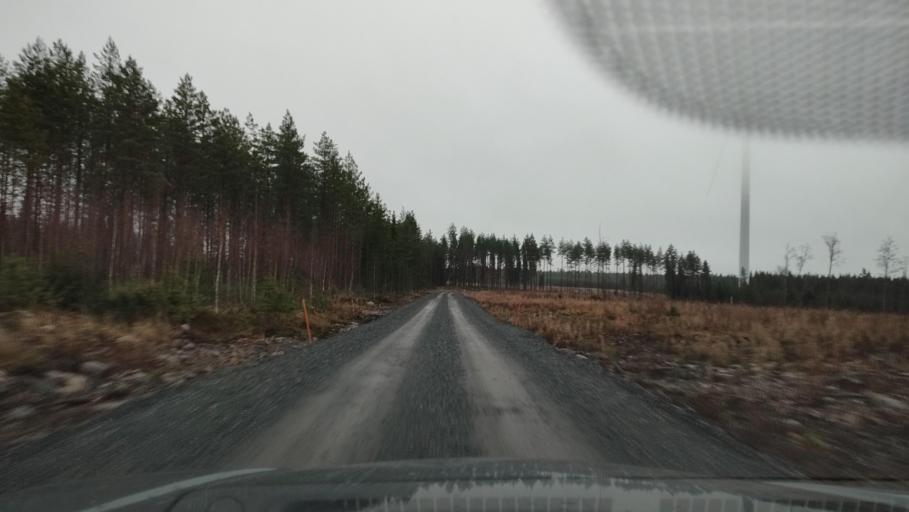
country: FI
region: Southern Ostrobothnia
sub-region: Suupohja
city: Karijoki
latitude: 62.1799
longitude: 21.5970
